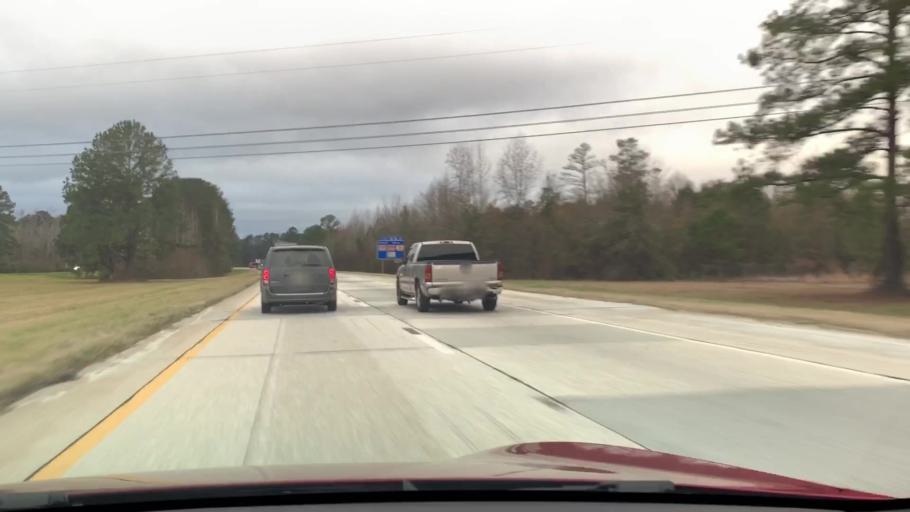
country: US
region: South Carolina
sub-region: Dillon County
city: Latta
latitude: 34.3532
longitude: -79.5200
